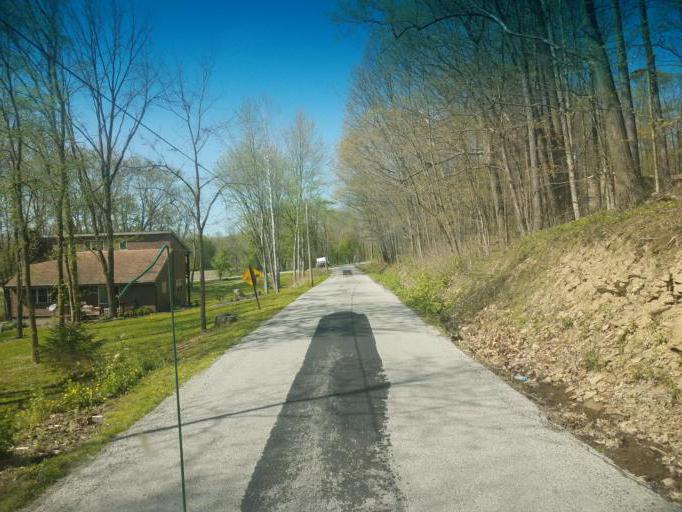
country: US
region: Ohio
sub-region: Medina County
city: Lodi
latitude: 40.9731
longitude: -82.0253
